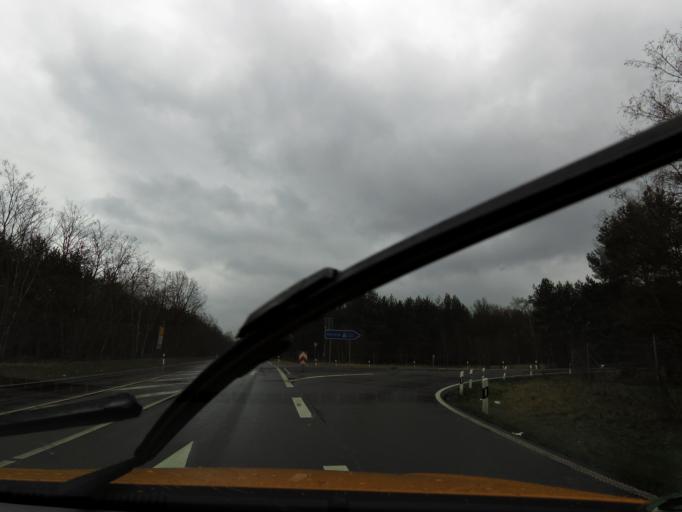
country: DE
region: Saxony-Anhalt
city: Loburg
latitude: 52.2351
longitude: 12.0619
